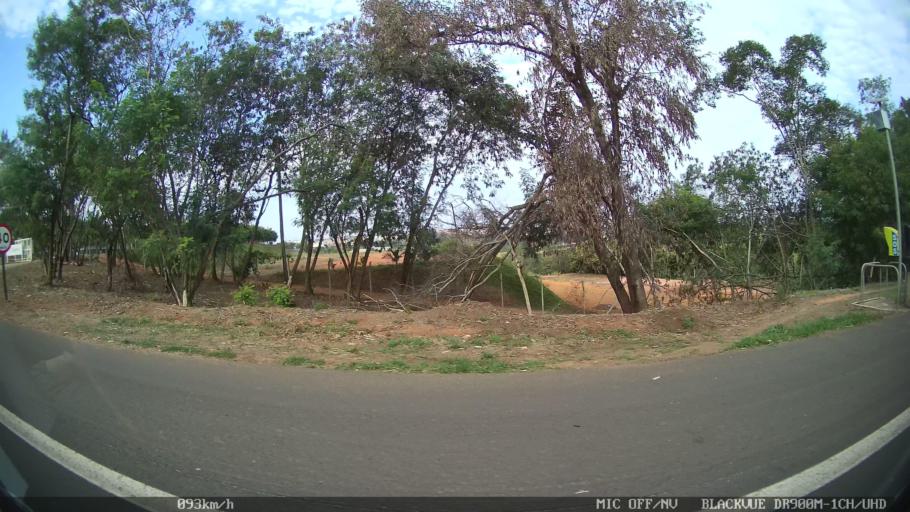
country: BR
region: Sao Paulo
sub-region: Cosmopolis
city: Cosmopolis
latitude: -22.6258
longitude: -47.2022
